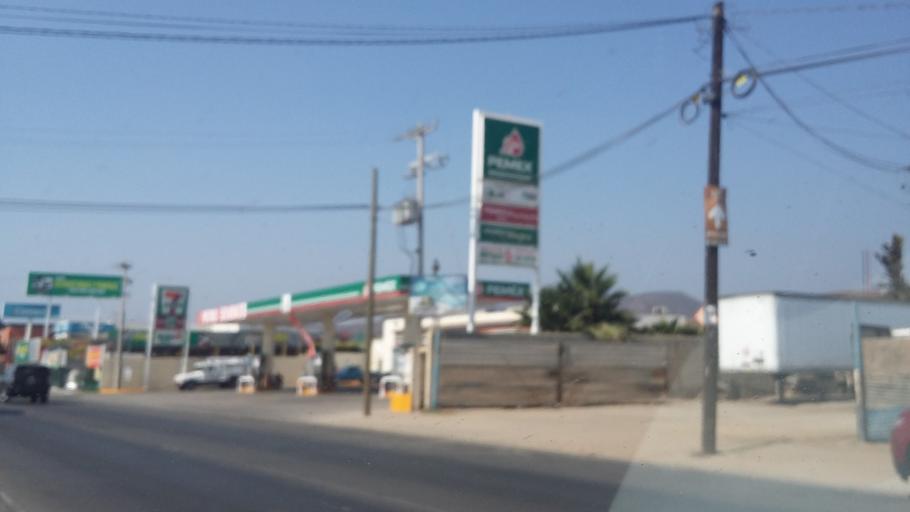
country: MX
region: Baja California
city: Ensenada
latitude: 31.7931
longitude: -116.5932
